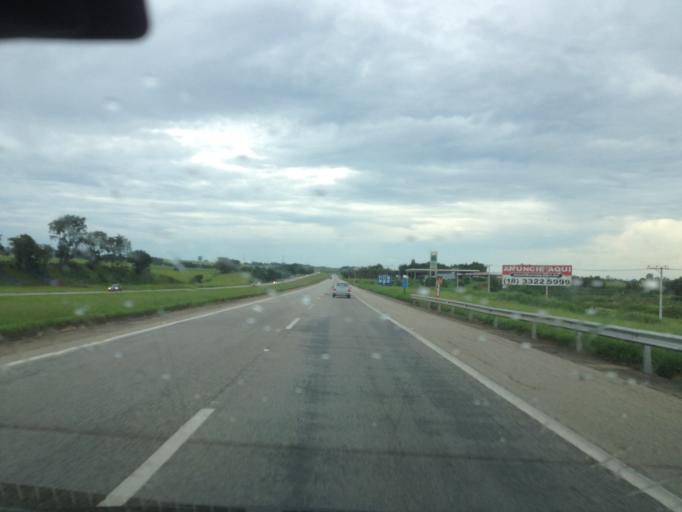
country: BR
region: Sao Paulo
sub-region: Porto Feliz
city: Porto Feliz
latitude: -23.3299
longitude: -47.5593
